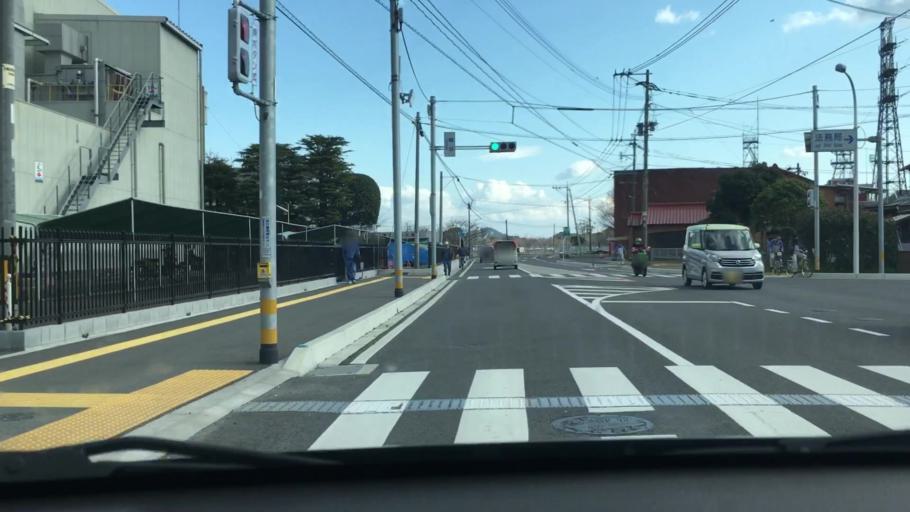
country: JP
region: Oita
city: Saiki
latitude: 32.9699
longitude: 131.9111
